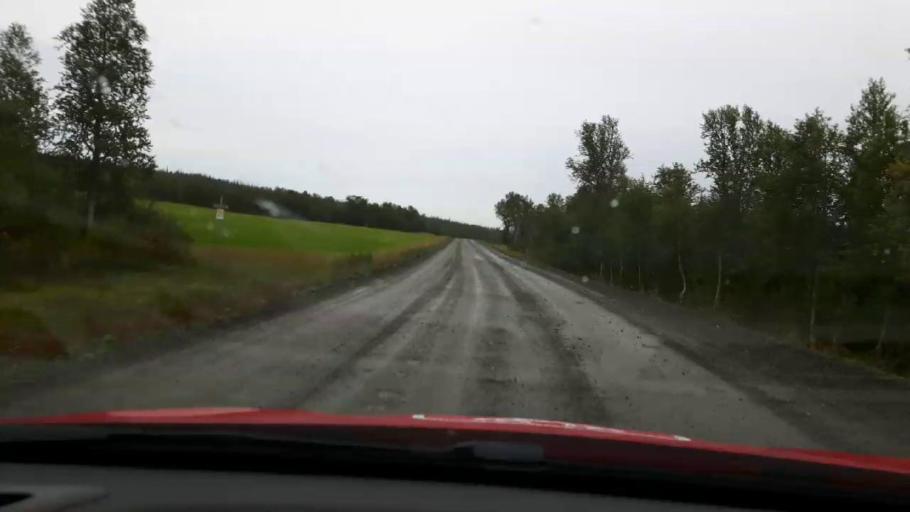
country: NO
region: Nord-Trondelag
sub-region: Meraker
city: Meraker
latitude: 63.5801
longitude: 12.2694
